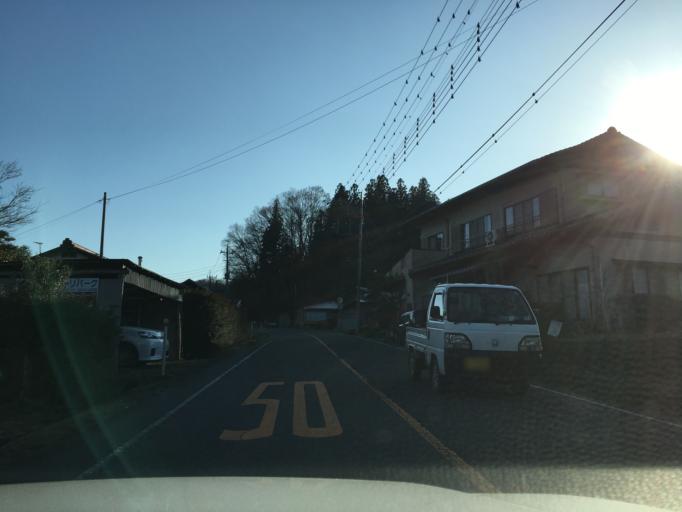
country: JP
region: Ibaraki
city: Daigo
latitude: 36.7774
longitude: 140.2640
